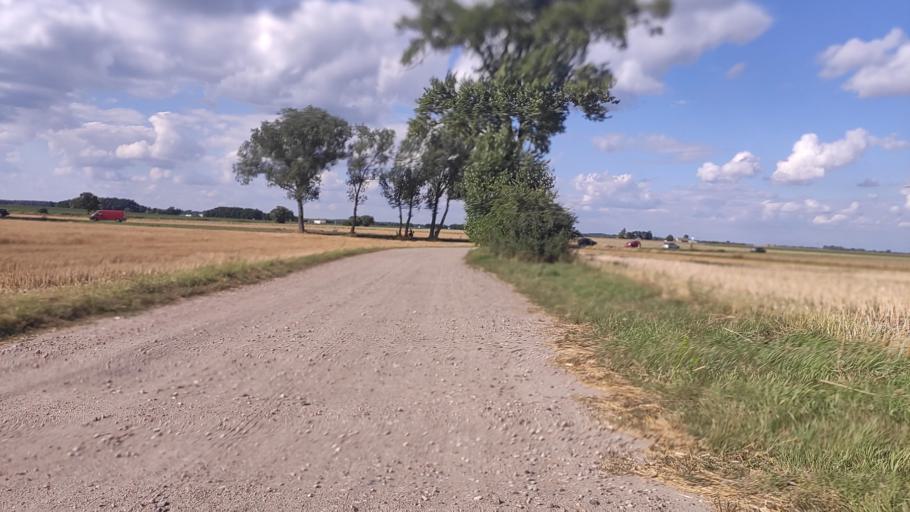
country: PL
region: Greater Poland Voivodeship
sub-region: Powiat poznanski
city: Swarzedz
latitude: 52.4187
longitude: 17.1417
